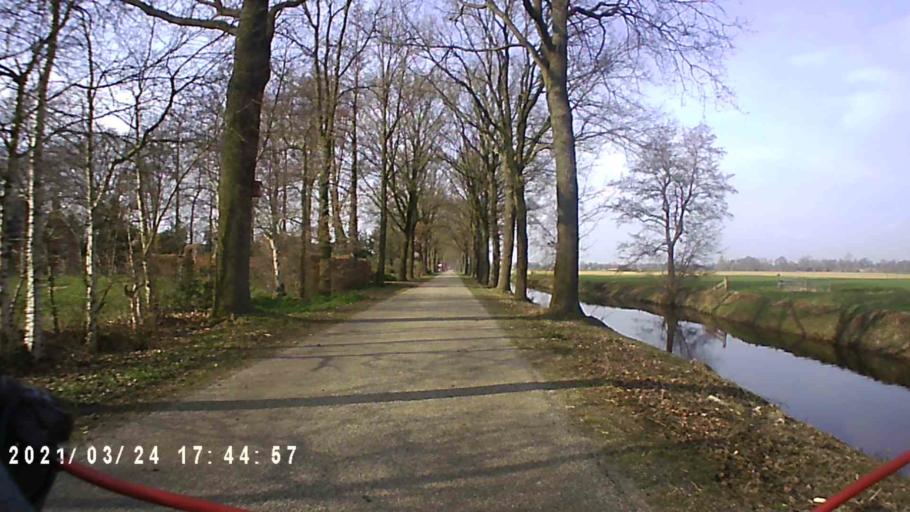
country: NL
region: Groningen
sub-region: Gemeente Leek
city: Leek
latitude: 53.1061
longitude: 6.3382
